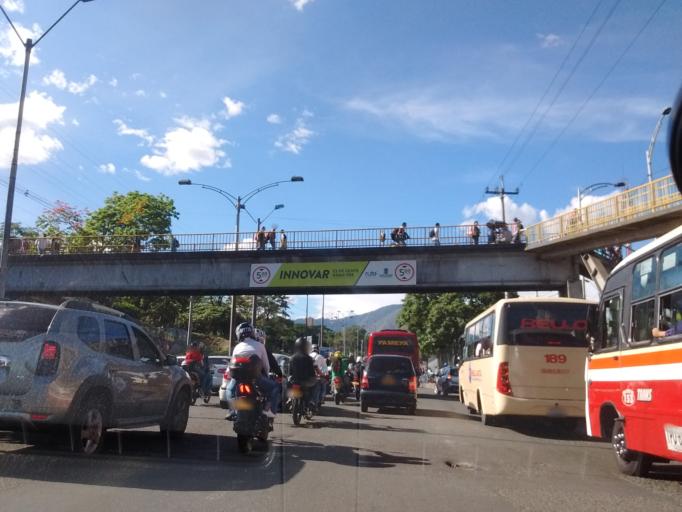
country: CO
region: Antioquia
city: Medellin
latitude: 6.2793
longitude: -75.5719
